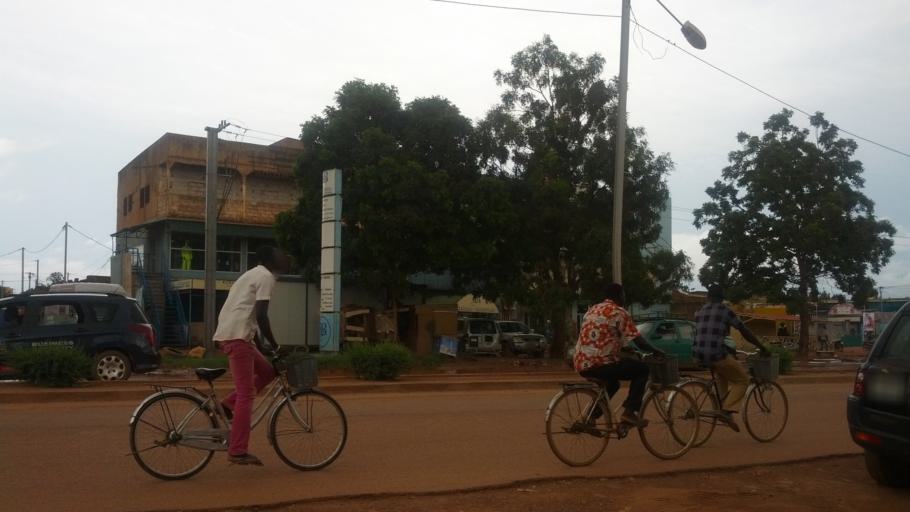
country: BF
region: Centre
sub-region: Kadiogo Province
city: Ouagadougou
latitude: 12.3518
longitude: -1.4883
